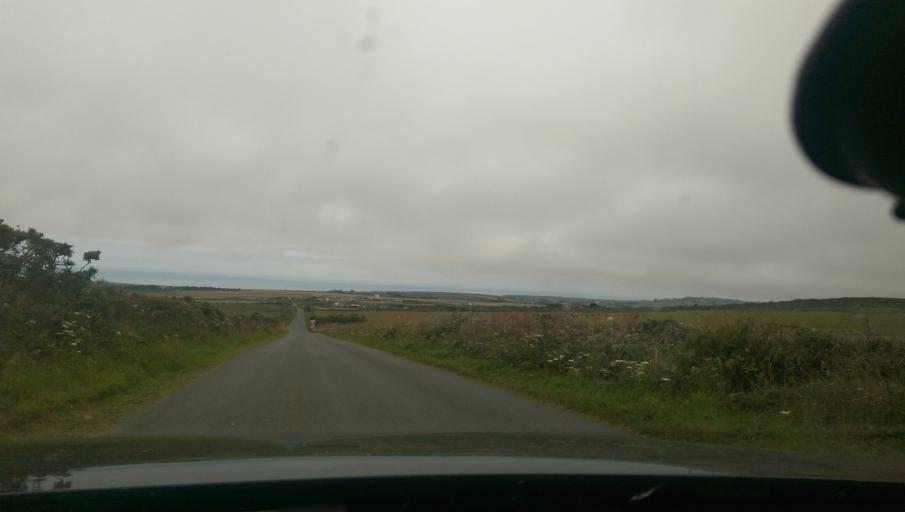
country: GB
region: England
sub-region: Cornwall
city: St. Buryan
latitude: 50.0979
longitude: -5.6535
